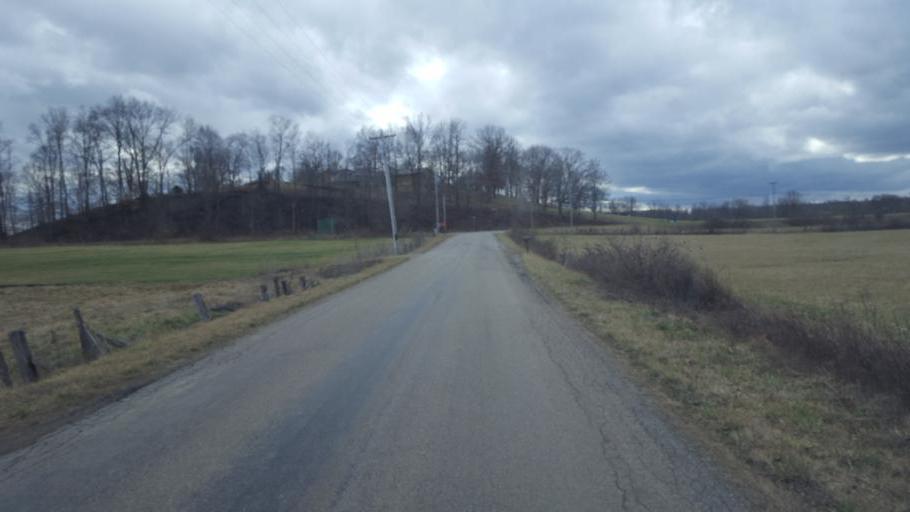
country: US
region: Ohio
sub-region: Muskingum County
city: Frazeysburg
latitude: 40.0954
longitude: -82.2004
